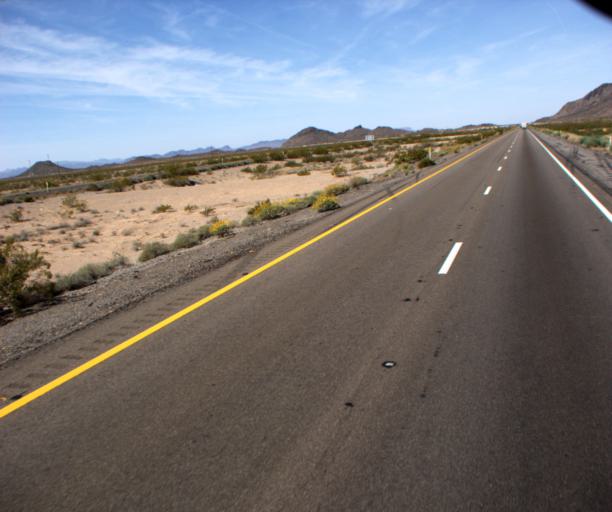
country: US
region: Arizona
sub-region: La Paz County
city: Salome
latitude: 33.6063
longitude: -113.5994
